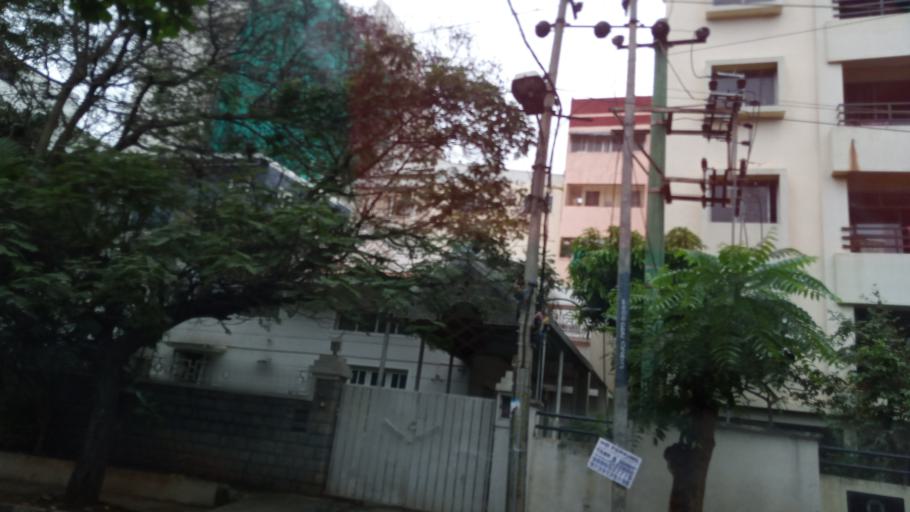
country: IN
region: Karnataka
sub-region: Bangalore Urban
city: Bangalore
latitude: 12.9389
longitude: 77.5392
